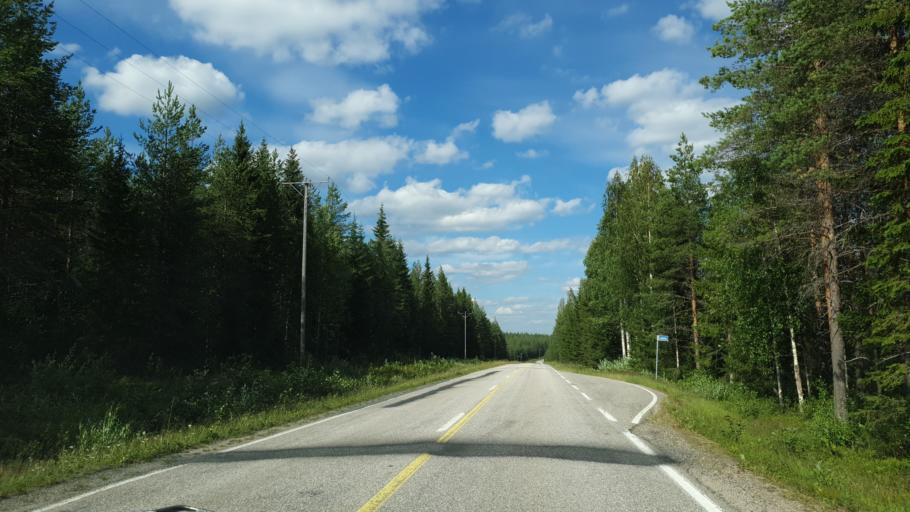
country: FI
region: Kainuu
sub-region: Kajaani
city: Sotkamo
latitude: 64.1917
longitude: 28.8961
